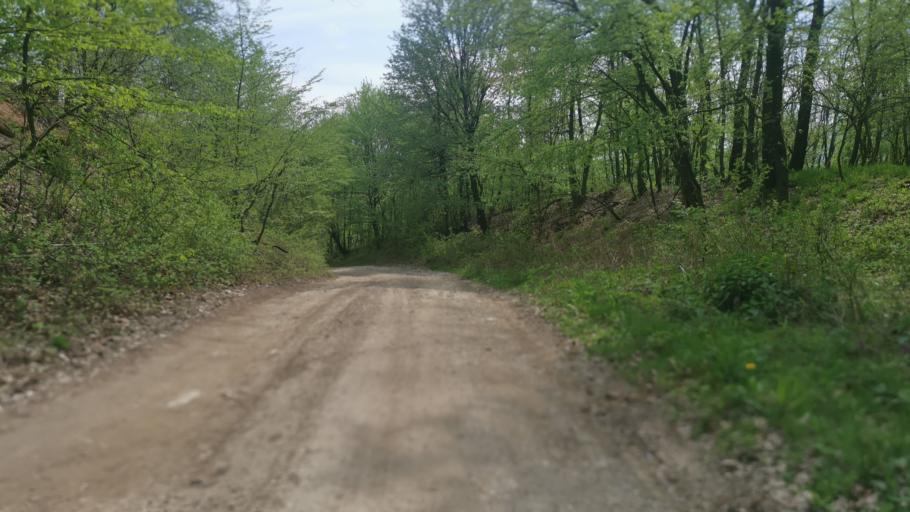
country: SK
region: Trnavsky
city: Smolenice
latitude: 48.5512
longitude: 17.4418
